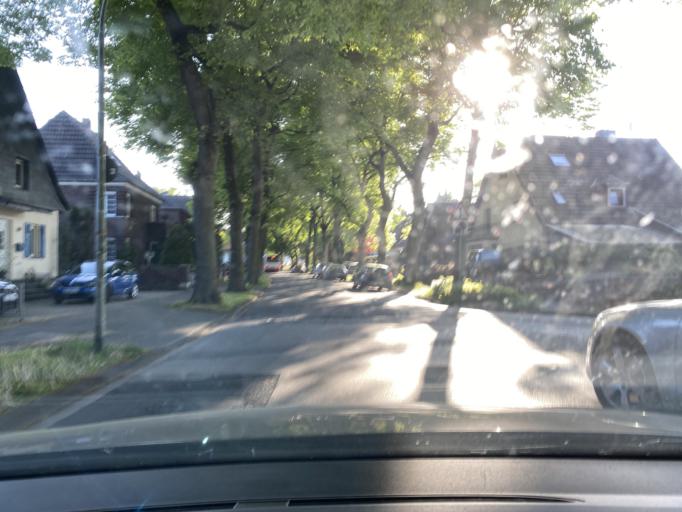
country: DE
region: North Rhine-Westphalia
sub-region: Regierungsbezirk Dusseldorf
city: Moers
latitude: 51.4865
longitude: 6.6693
